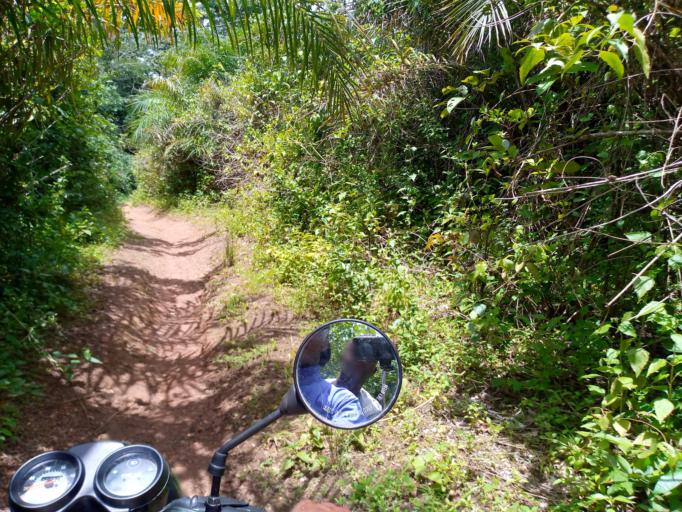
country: SL
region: Northern Province
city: Mange
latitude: 8.9792
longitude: -12.7466
